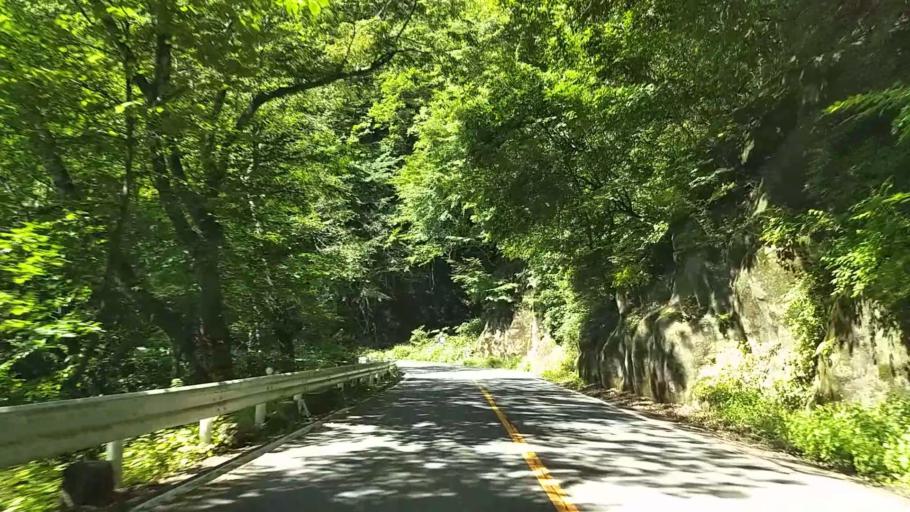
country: JP
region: Nagano
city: Saku
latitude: 36.3490
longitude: 138.6552
